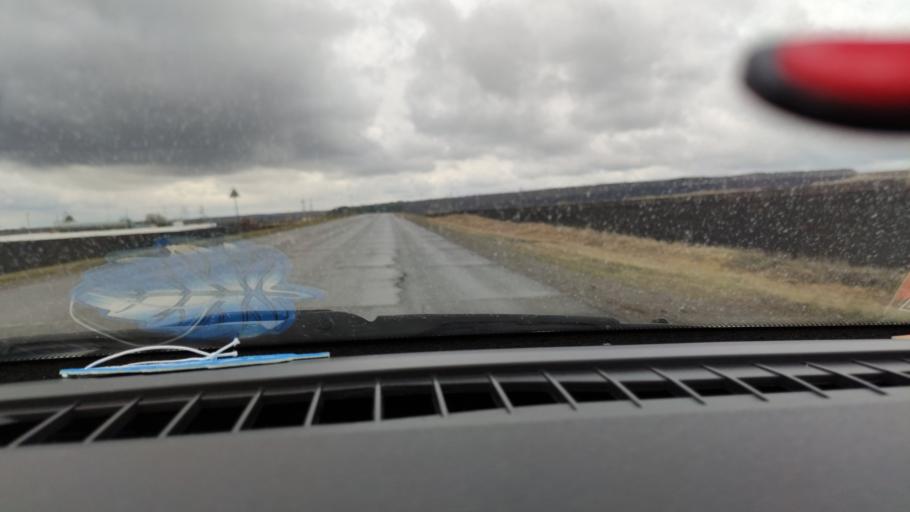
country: RU
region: Tatarstan
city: Nurlat
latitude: 54.3909
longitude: 50.7617
